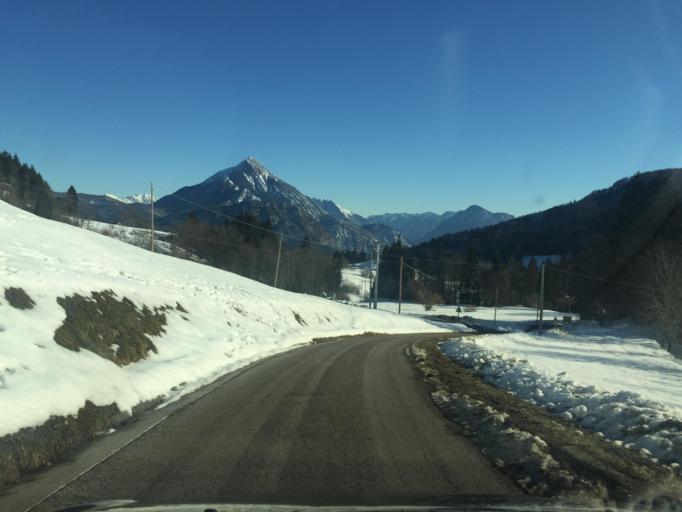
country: IT
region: Friuli Venezia Giulia
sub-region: Provincia di Udine
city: Lauco
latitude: 46.4301
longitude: 12.9745
